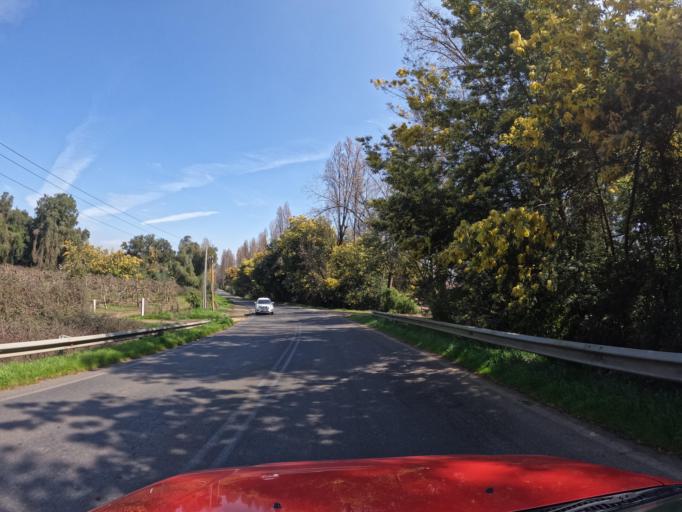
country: CL
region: Maule
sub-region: Provincia de Talca
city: San Clemente
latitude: -35.4865
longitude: -71.2906
